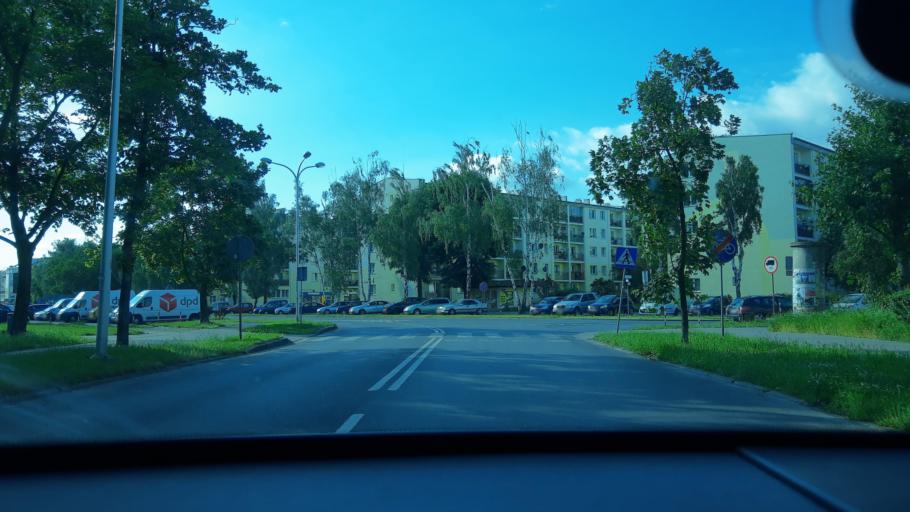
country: PL
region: Lodz Voivodeship
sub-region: Powiat sieradzki
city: Sieradz
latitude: 51.5892
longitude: 18.7313
